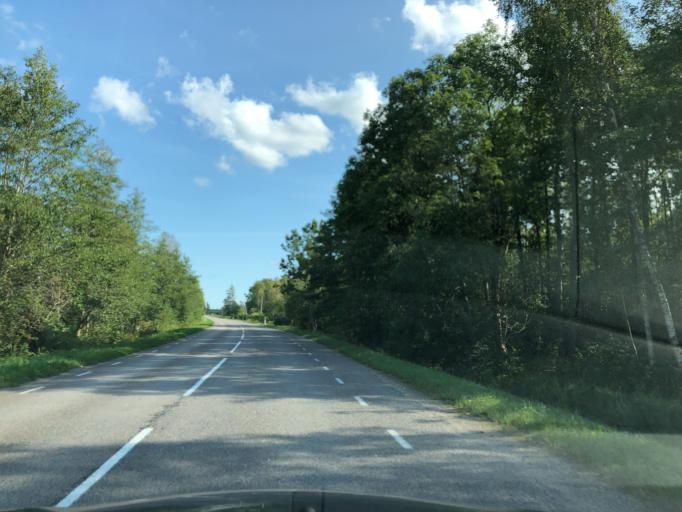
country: EE
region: Hiiumaa
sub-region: Kaerdla linn
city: Kardla
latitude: 58.7187
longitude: 22.5653
